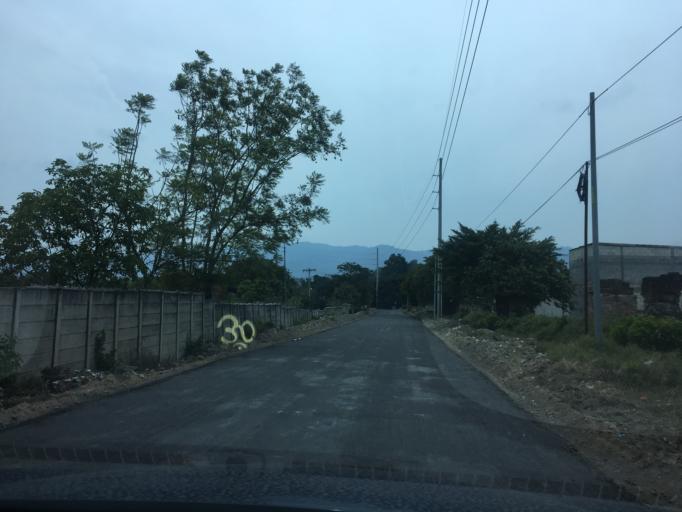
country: GT
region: Guatemala
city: Petapa
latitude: 14.5148
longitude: -90.5526
